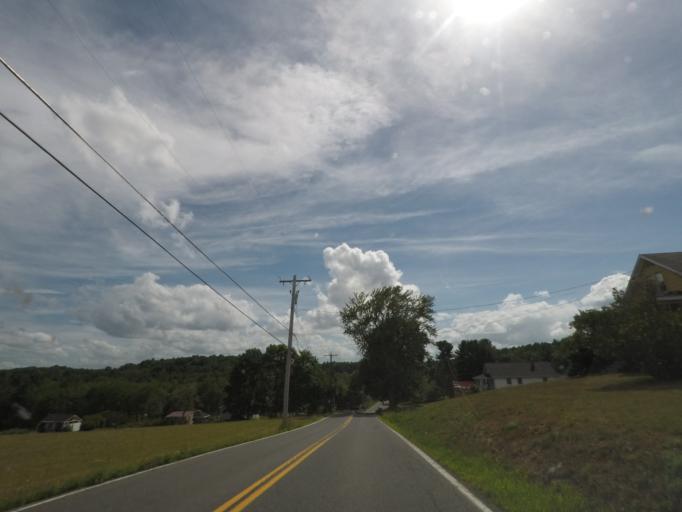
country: US
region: New York
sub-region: Rensselaer County
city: Wynantskill
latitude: 42.7101
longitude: -73.6076
